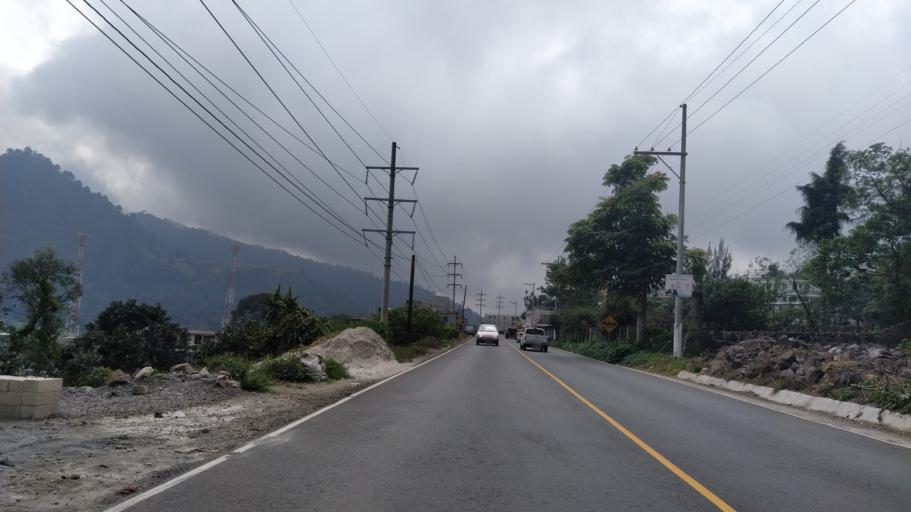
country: GT
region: Quetzaltenango
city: Zunil
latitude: 14.7508
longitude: -91.5099
